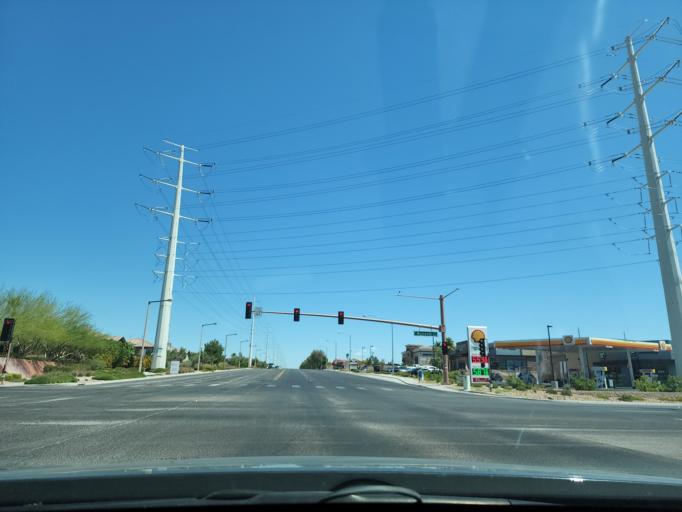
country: US
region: Nevada
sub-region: Clark County
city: Summerlin South
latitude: 36.0849
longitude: -115.3155
